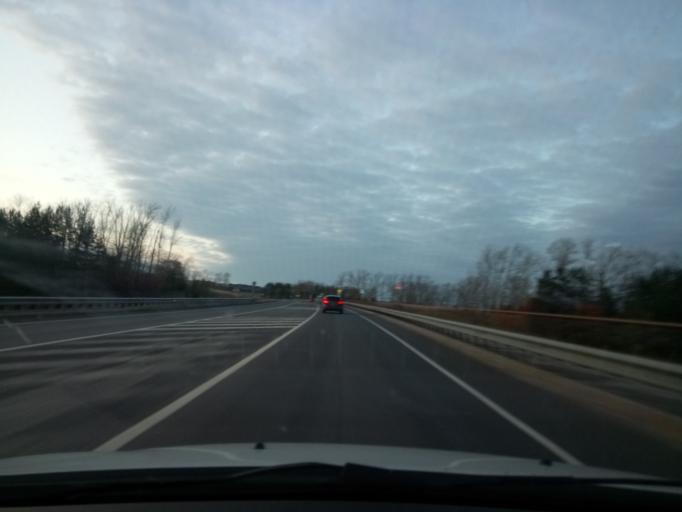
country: RU
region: Nizjnij Novgorod
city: Bol'shoye Murashkino
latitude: 55.8847
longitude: 44.7474
